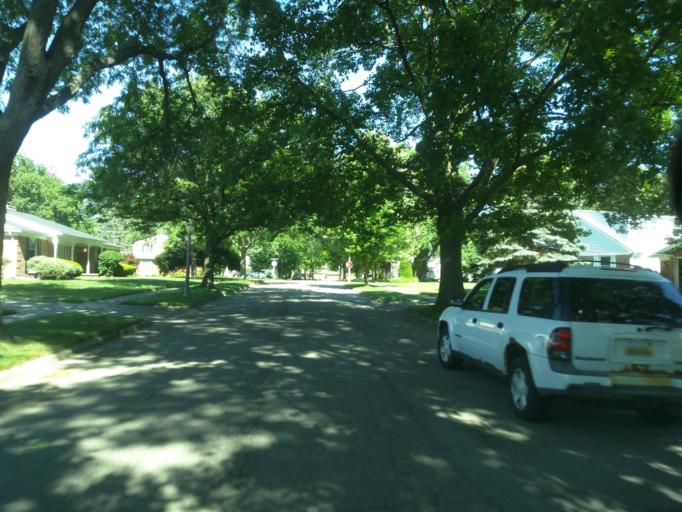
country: US
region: Michigan
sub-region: Ingham County
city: Edgemont Park
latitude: 42.7587
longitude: -84.5992
